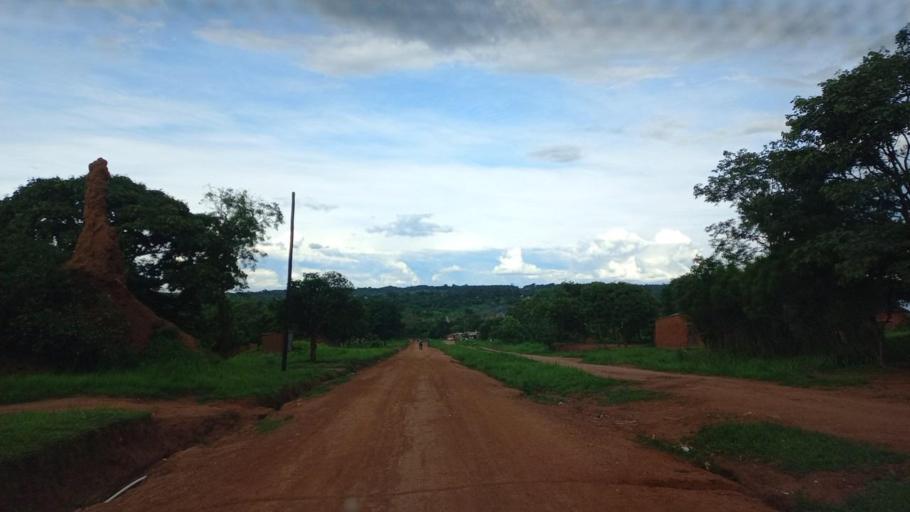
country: ZM
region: North-Western
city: Mwinilunga
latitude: -11.7566
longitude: 24.4325
